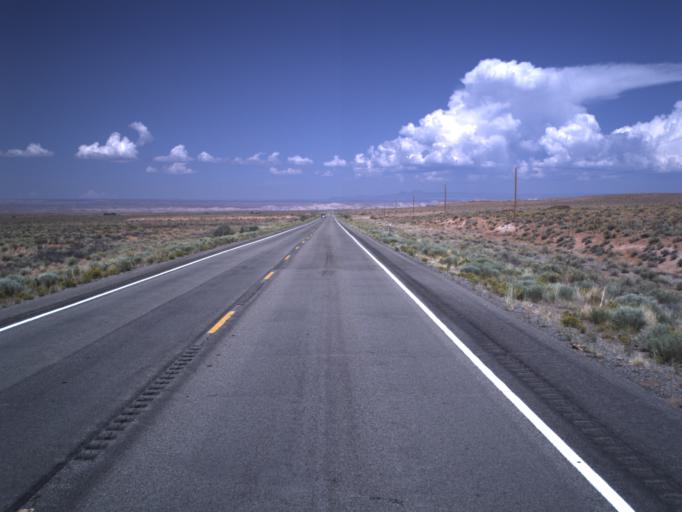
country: US
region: Utah
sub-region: San Juan County
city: Blanding
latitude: 37.1276
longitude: -109.5485
